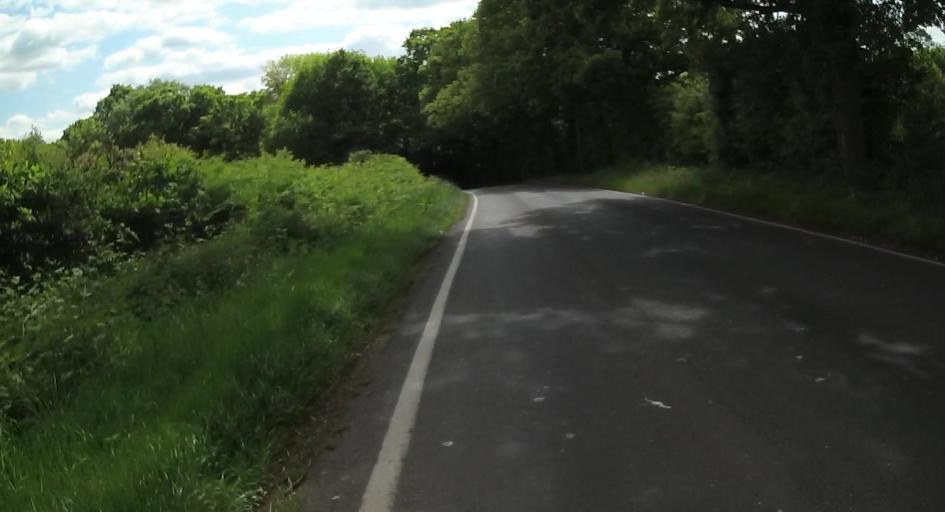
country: GB
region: England
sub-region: Surrey
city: Farnham
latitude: 51.2248
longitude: -0.8382
